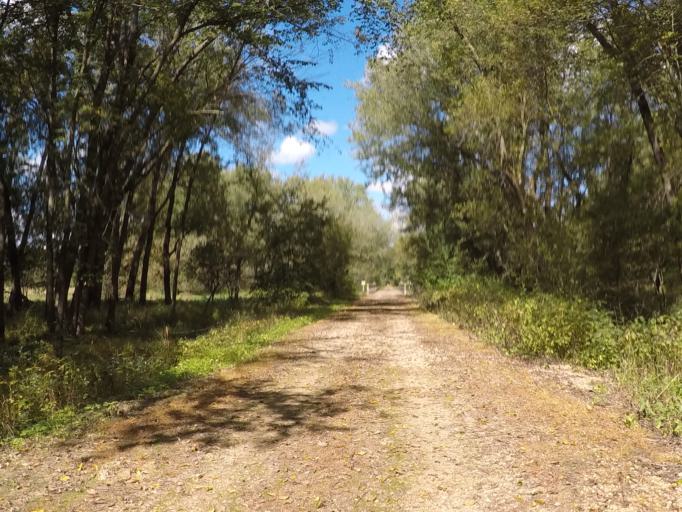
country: US
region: Wisconsin
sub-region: Richland County
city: Richland Center
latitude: 43.2839
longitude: -90.3196
